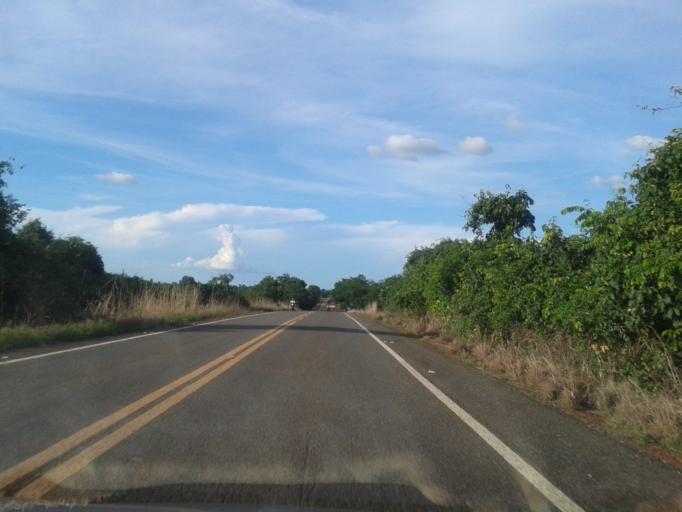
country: BR
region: Goias
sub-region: Sao Miguel Do Araguaia
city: Sao Miguel do Araguaia
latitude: -13.7017
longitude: -50.3323
